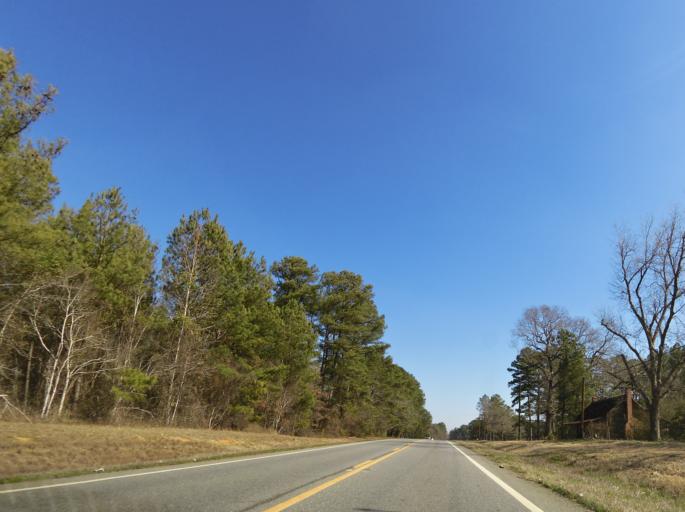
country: US
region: Georgia
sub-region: Bleckley County
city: Cochran
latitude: 32.3658
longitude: -83.3798
